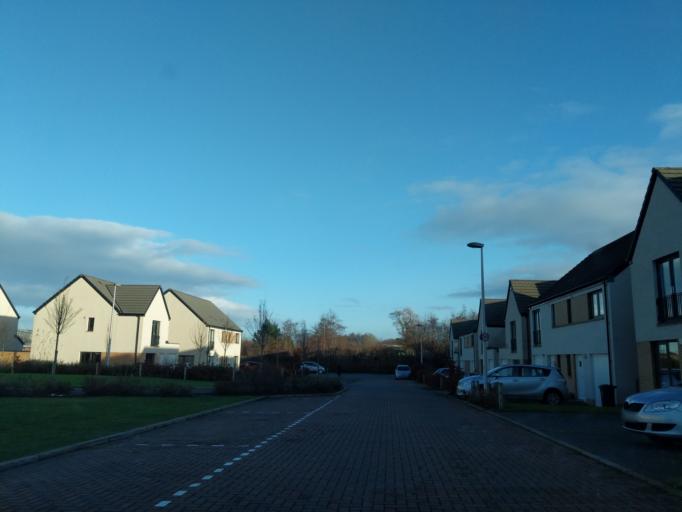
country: GB
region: Scotland
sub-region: Edinburgh
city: Colinton
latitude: 55.9271
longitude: -3.2758
